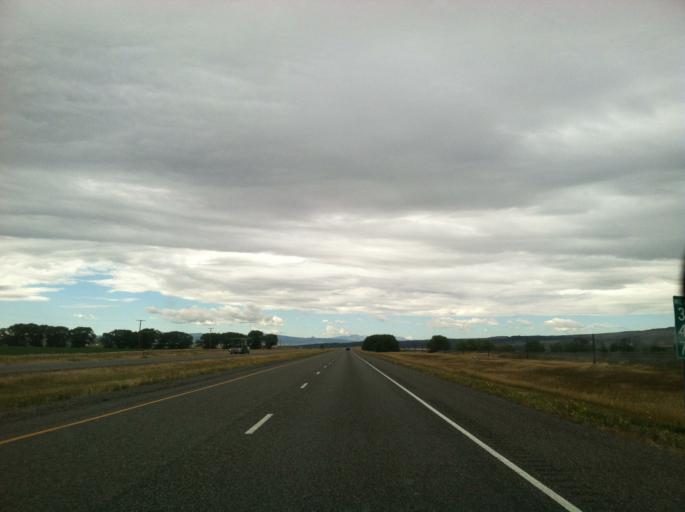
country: US
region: Montana
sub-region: Park County
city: Livingston
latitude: 45.7006
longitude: -110.3255
